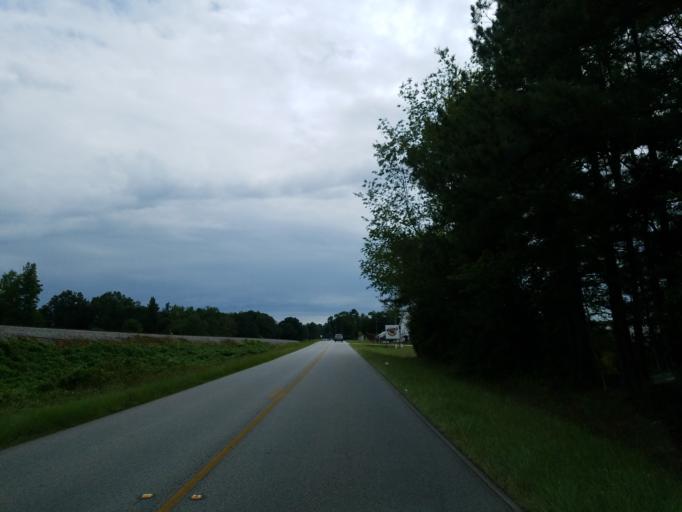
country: US
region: Georgia
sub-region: Spalding County
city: Experiment
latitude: 33.3075
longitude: -84.2890
